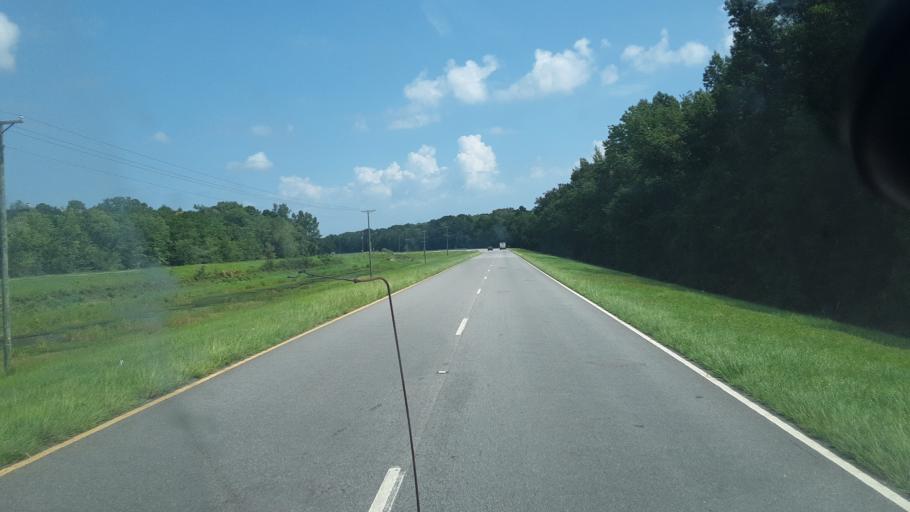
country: US
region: South Carolina
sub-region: Bamberg County
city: Bamberg
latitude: 33.3323
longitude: -81.0209
